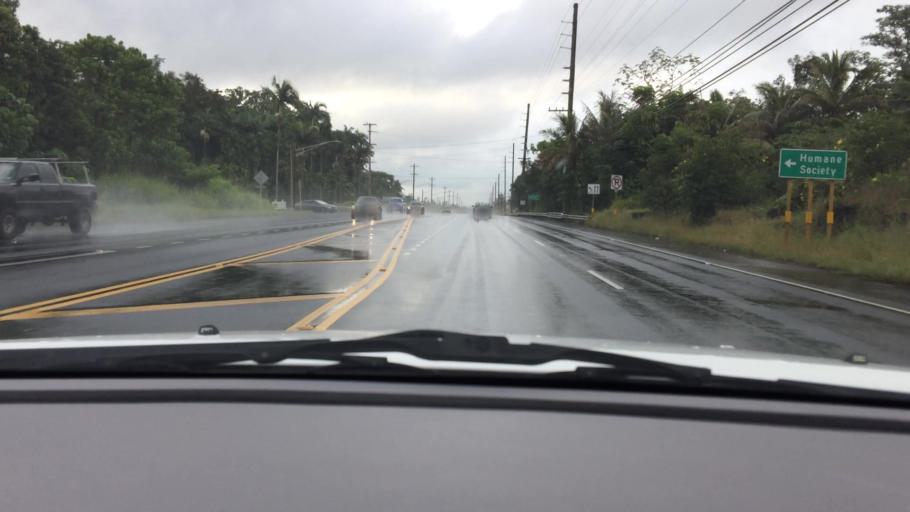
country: US
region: Hawaii
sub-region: Hawaii County
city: Kea'au
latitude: 19.6055
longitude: -155.0271
